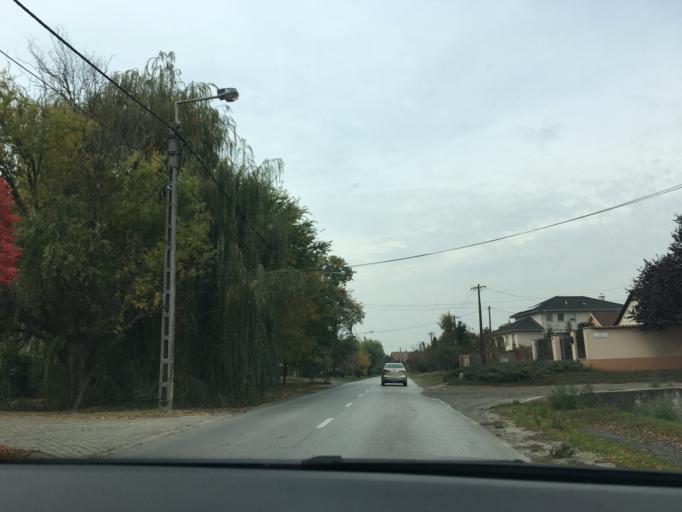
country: HU
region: Hajdu-Bihar
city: Debrecen
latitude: 47.5500
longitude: 21.6749
